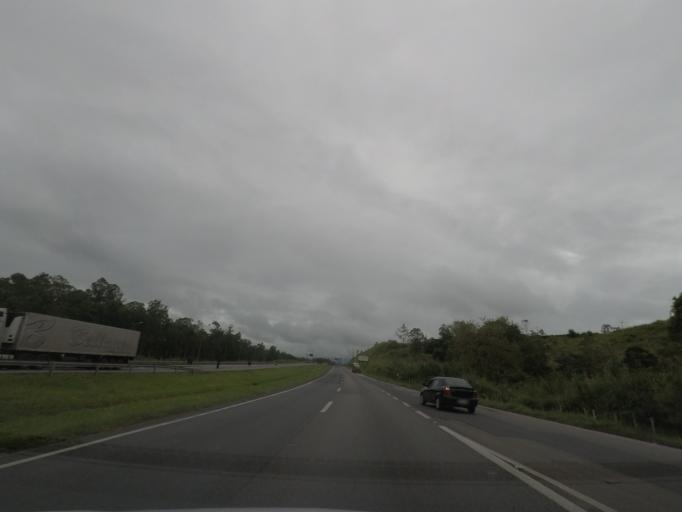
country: BR
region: Sao Paulo
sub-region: Cajati
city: Cajati
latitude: -24.7302
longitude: -48.0964
